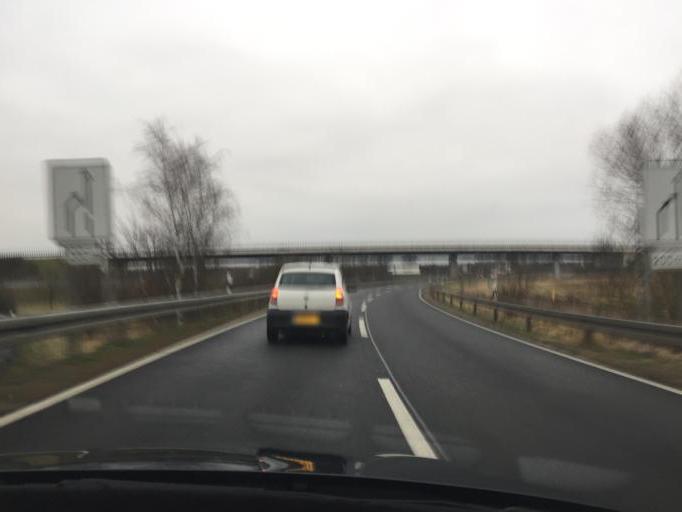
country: DE
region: Brandenburg
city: Schulzendorf
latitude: 52.3179
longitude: 13.5525
